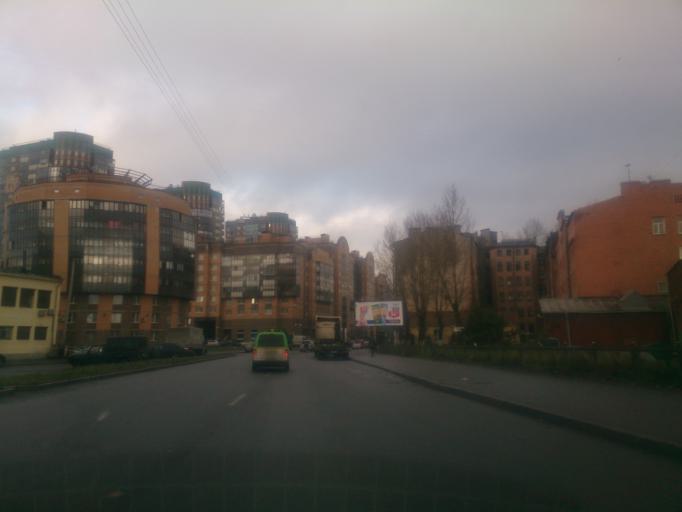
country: RU
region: St.-Petersburg
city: Admiralteisky
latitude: 59.9033
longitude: 30.2907
